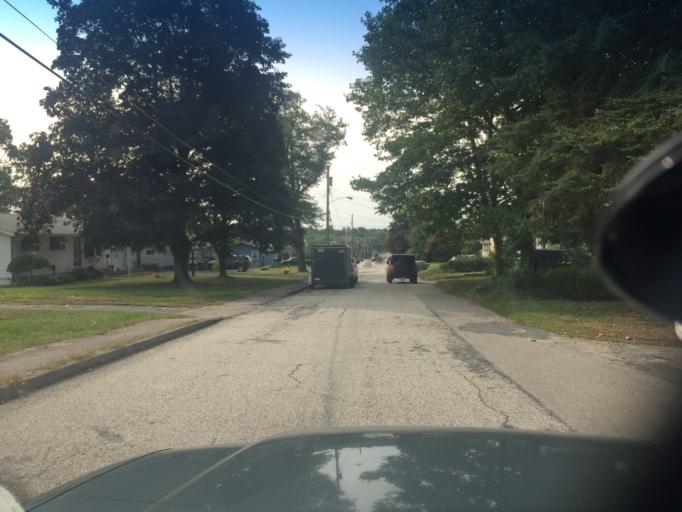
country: US
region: Massachusetts
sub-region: Norfolk County
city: Bellingham
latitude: 42.1157
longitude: -71.4726
